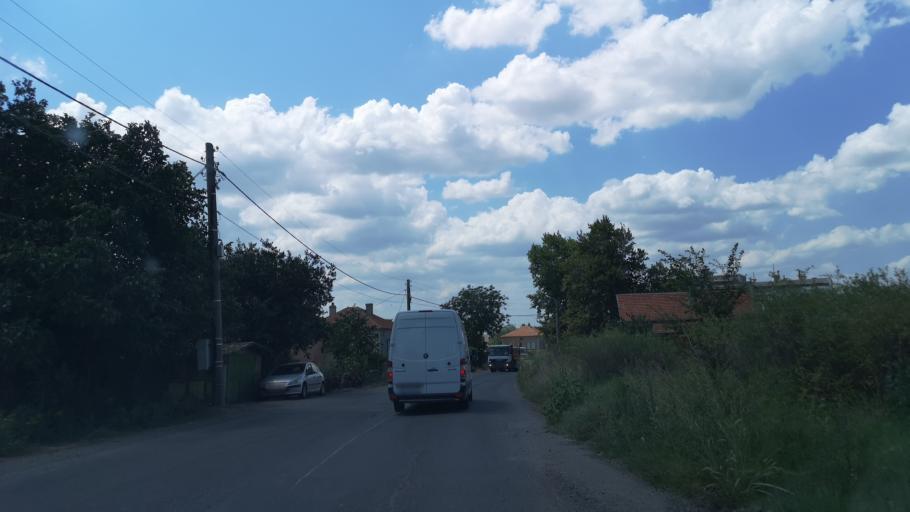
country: BG
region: Burgas
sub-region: Obshtina Kameno
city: Kameno
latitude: 42.6159
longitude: 27.3072
